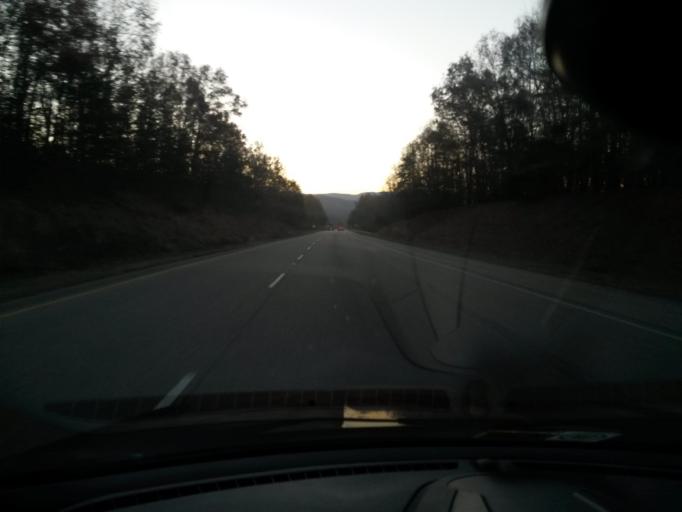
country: US
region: Virginia
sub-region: Alleghany County
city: Clifton Forge
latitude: 37.8281
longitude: -79.7530
